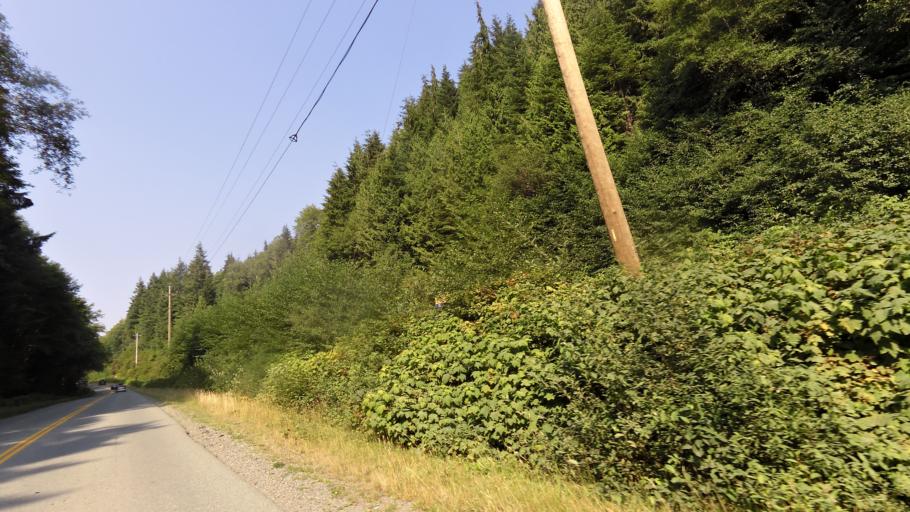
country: CA
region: British Columbia
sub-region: Regional District of Alberni-Clayoquot
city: Ucluelet
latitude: 49.0564
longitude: -125.4780
